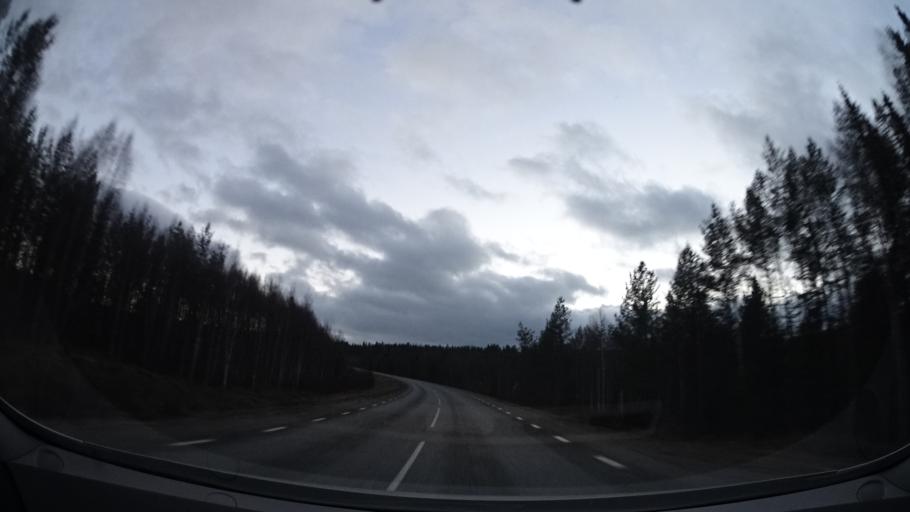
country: SE
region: Vaesterbotten
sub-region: Asele Kommun
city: Asele
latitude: 64.2096
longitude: 17.5129
